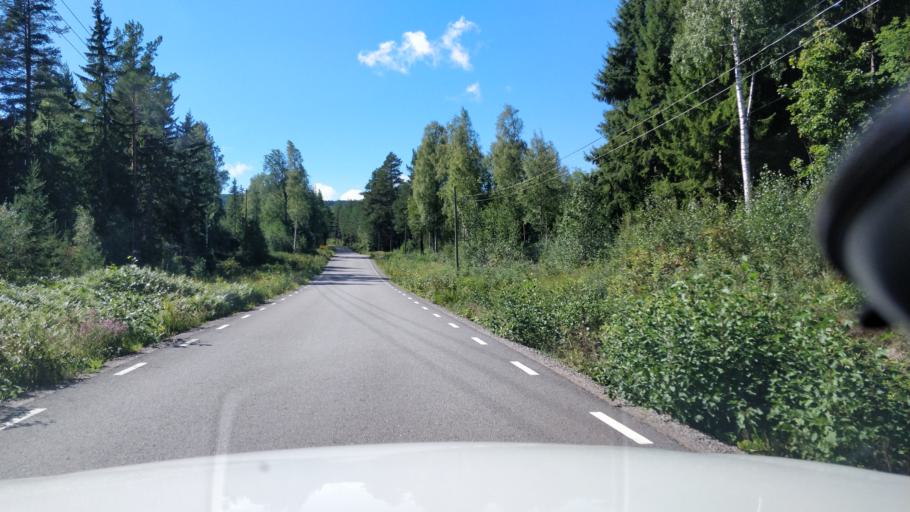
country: SE
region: Dalarna
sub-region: Faluns Kommun
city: Bjursas
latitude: 60.7517
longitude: 15.4961
